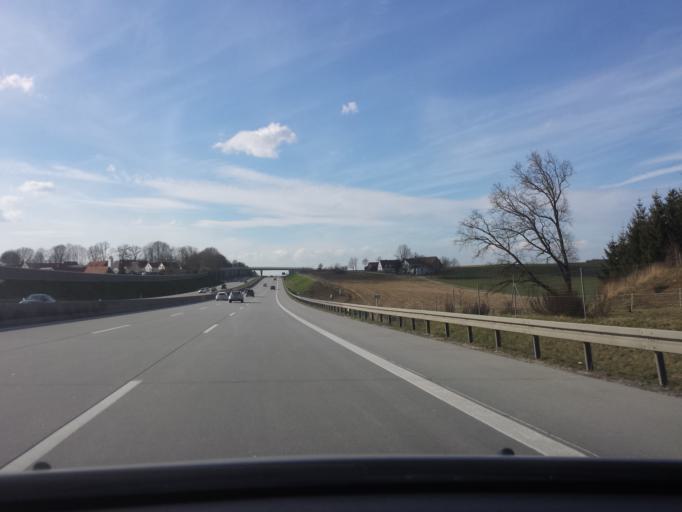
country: DE
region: Bavaria
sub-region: Swabia
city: Adelzhausen
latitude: 48.3712
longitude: 11.1007
